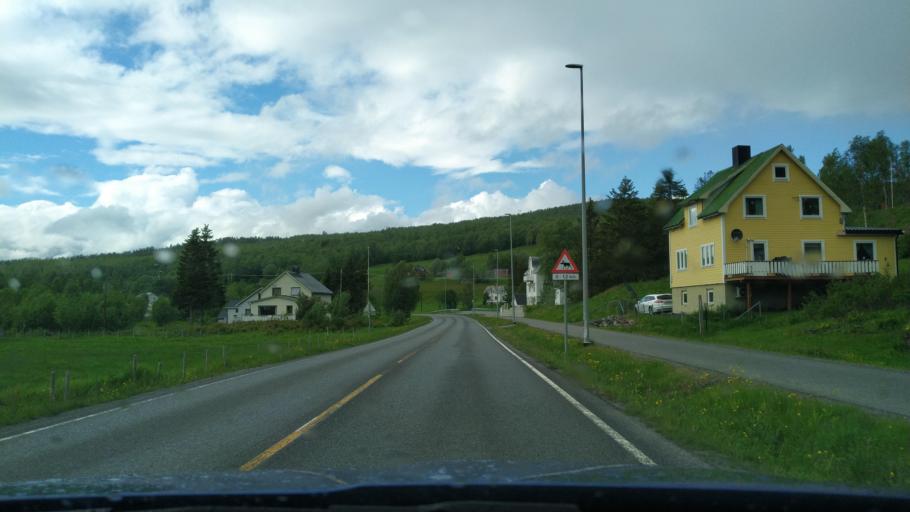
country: NO
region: Troms
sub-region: Sorreisa
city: Sorreisa
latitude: 69.1708
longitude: 18.1143
